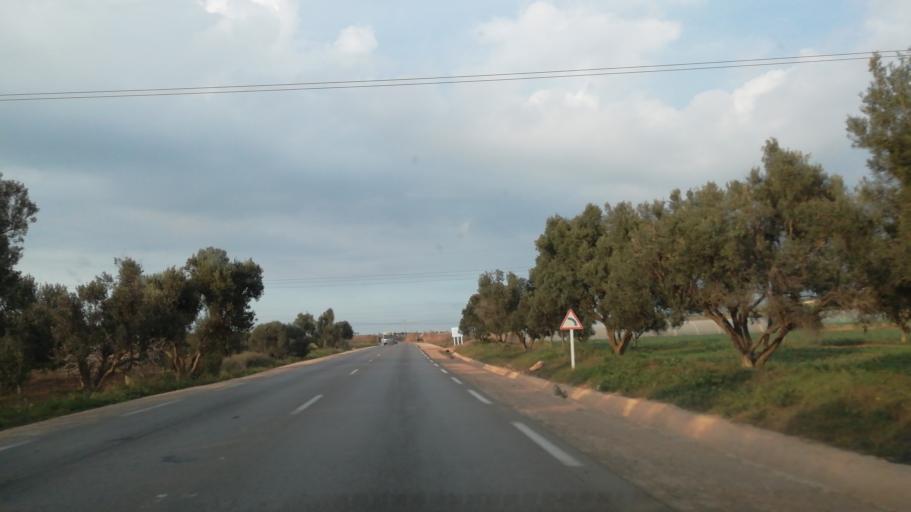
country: DZ
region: Oran
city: Ain el Bya
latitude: 35.7768
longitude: -0.0971
